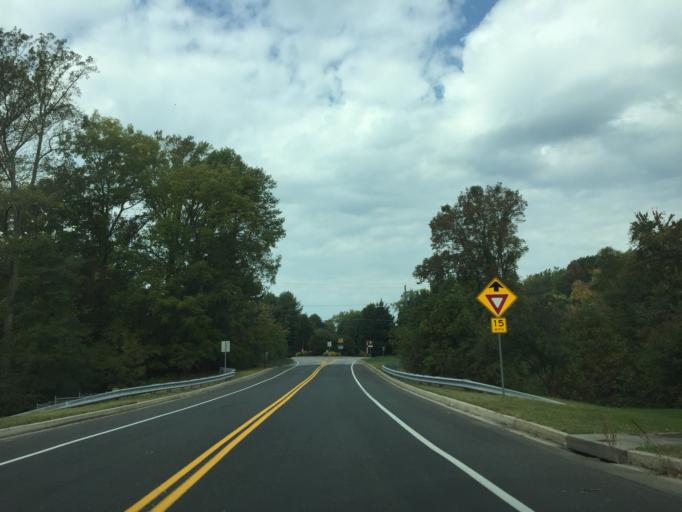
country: US
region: Maryland
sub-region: Harford County
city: Bel Air South
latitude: 39.4933
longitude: -76.3153
